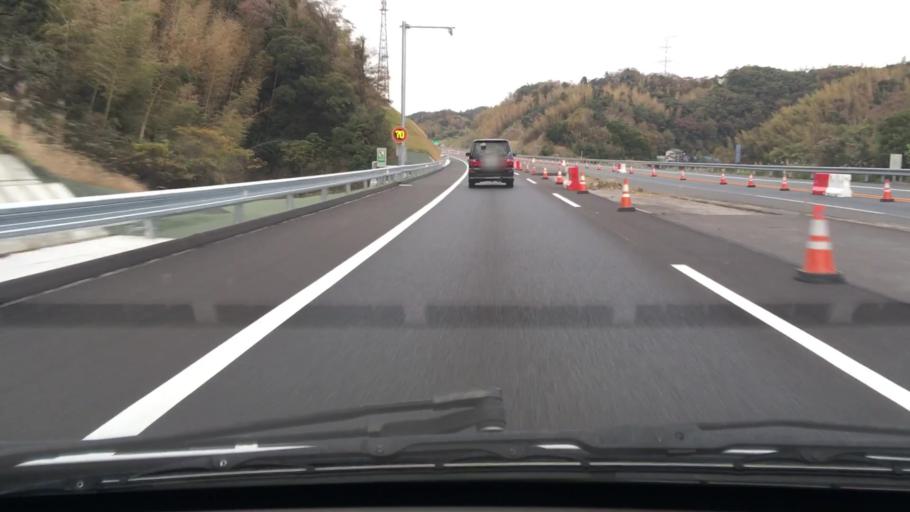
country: JP
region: Chiba
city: Kimitsu
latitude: 35.2768
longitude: 139.9222
